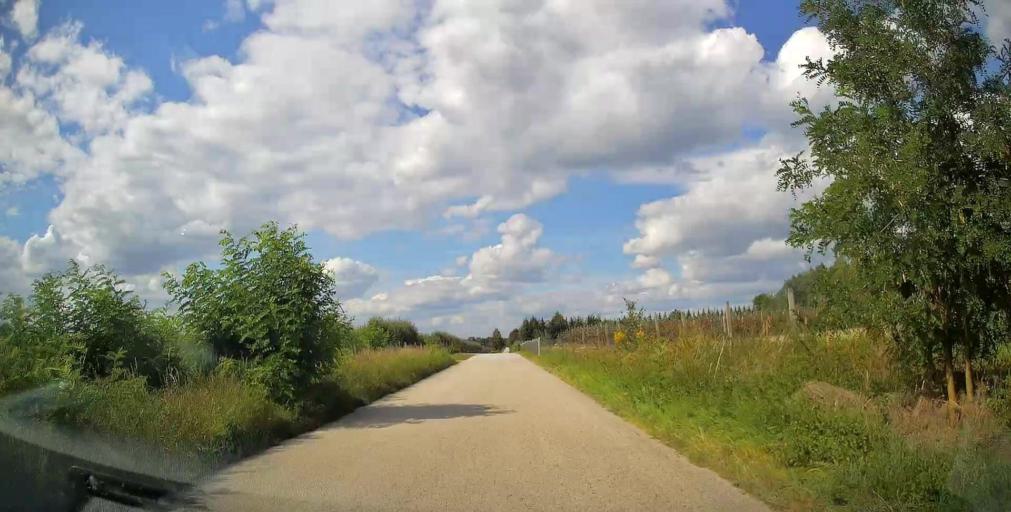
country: PL
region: Masovian Voivodeship
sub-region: Powiat grojecki
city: Goszczyn
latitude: 51.7038
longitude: 20.8969
